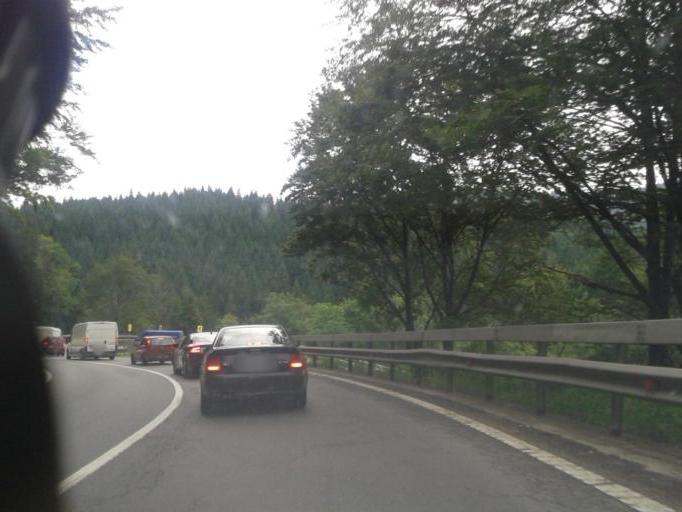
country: RO
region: Brasov
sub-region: Oras Predeal
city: Predeal
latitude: 45.5190
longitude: 25.5756
